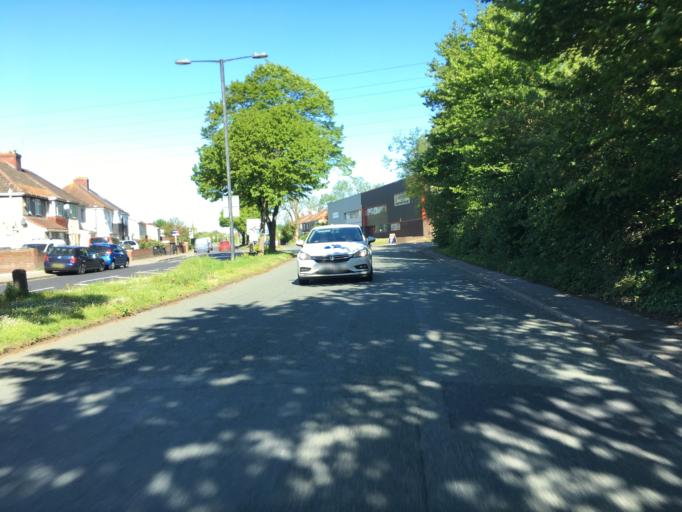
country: GB
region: England
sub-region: North Somerset
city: Easton-in-Gordano
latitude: 51.4971
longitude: -2.6870
